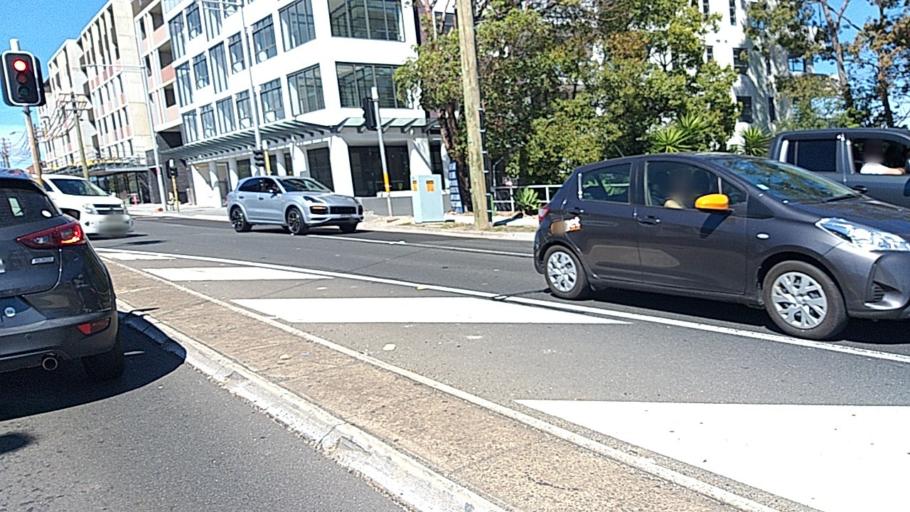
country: AU
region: New South Wales
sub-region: Hunters Hill
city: Gladesville
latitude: -33.8236
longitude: 151.1234
